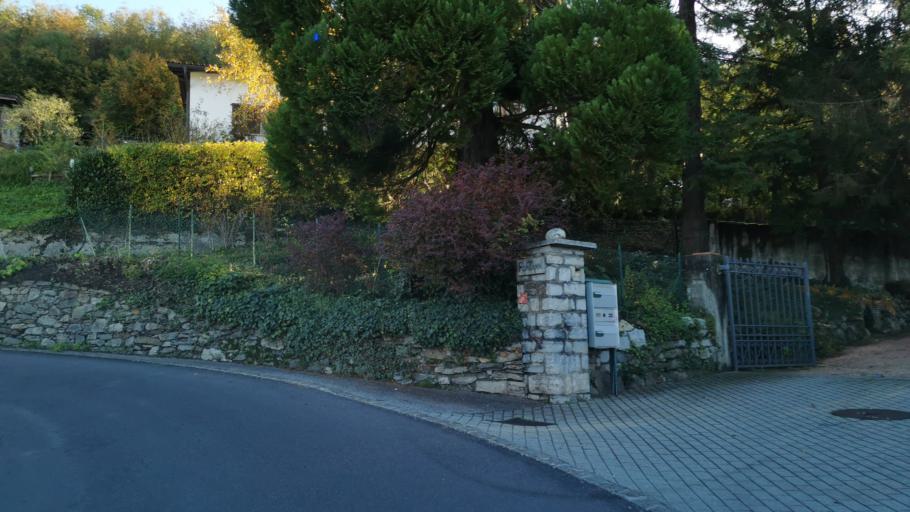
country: CH
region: Ticino
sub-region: Lugano District
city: Pura
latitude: 46.0056
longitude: 8.8589
